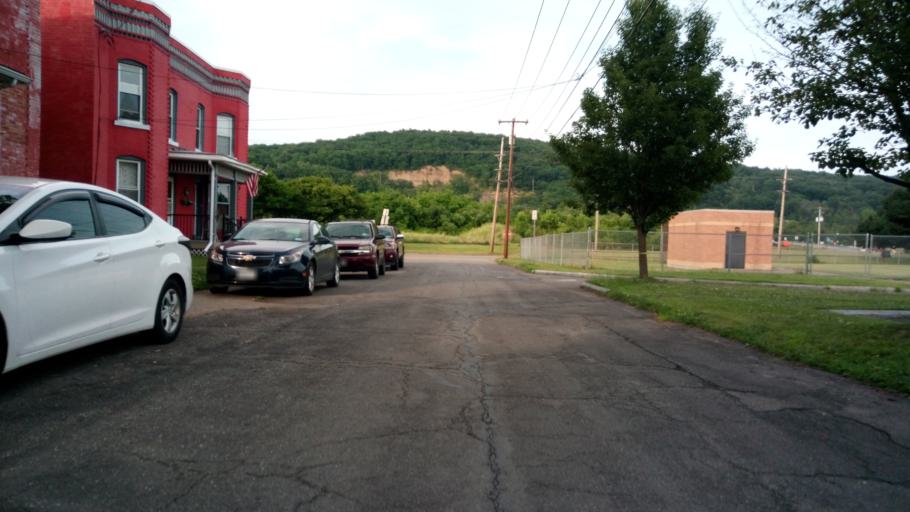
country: US
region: New York
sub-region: Chemung County
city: Elmira
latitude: 42.0958
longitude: -76.7934
